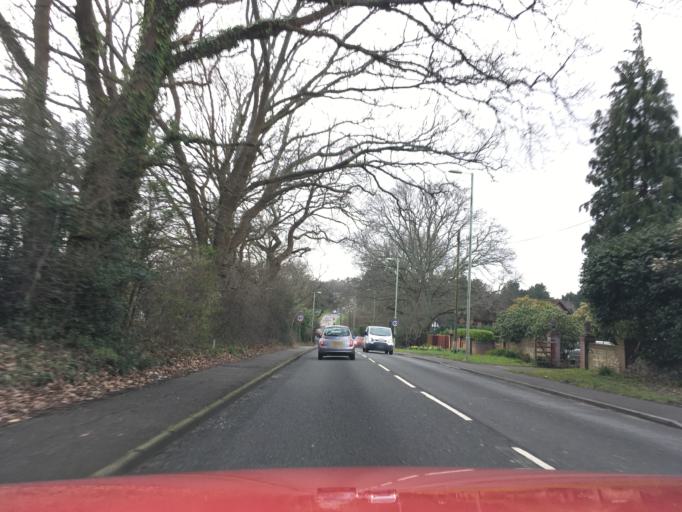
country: GB
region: England
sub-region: Hampshire
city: Eastleigh
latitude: 50.9722
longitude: -1.3893
